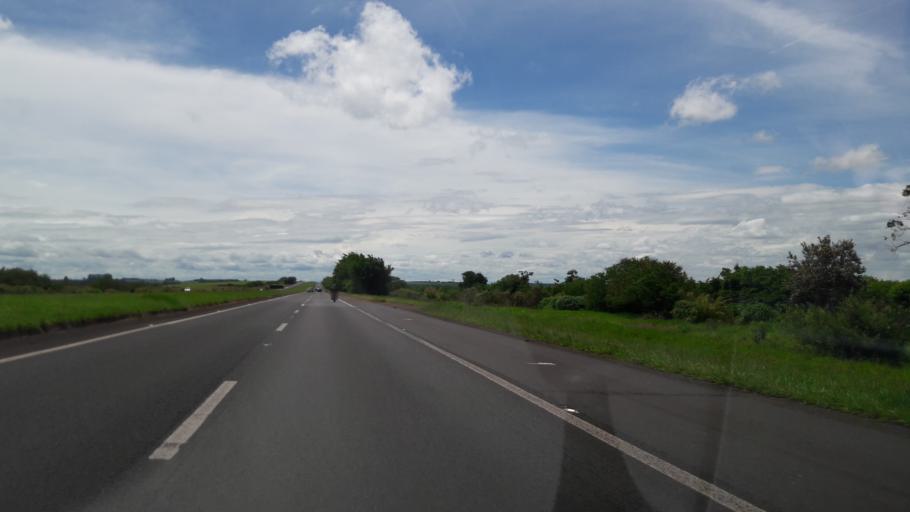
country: BR
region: Sao Paulo
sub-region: Avare
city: Avare
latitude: -22.9524
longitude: -48.8747
